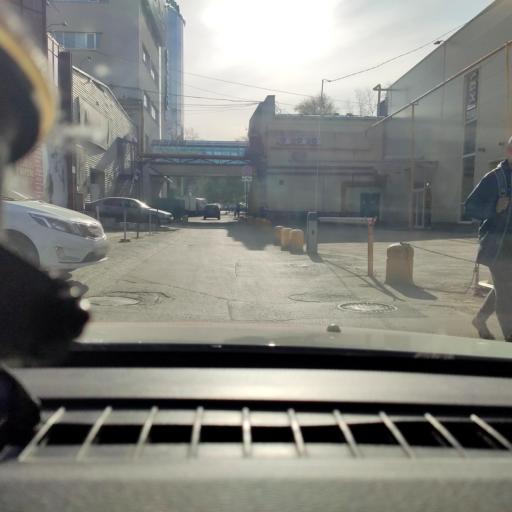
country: RU
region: Samara
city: Samara
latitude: 53.2041
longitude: 50.1458
